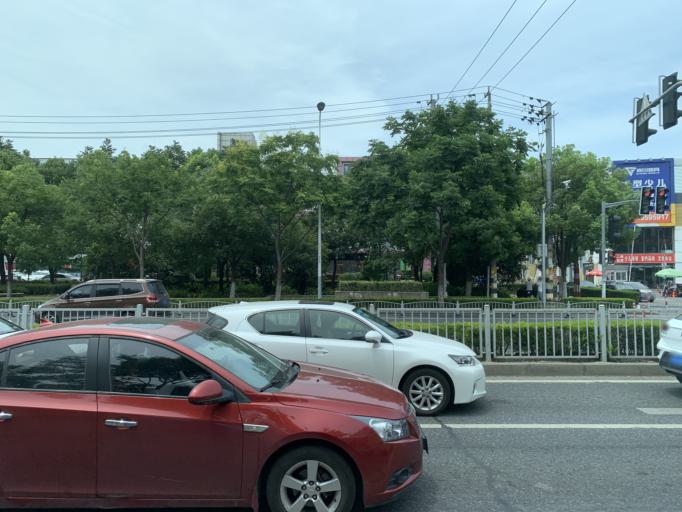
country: CN
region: Shanghai Shi
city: Kangqiao
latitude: 31.1567
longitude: 121.5605
